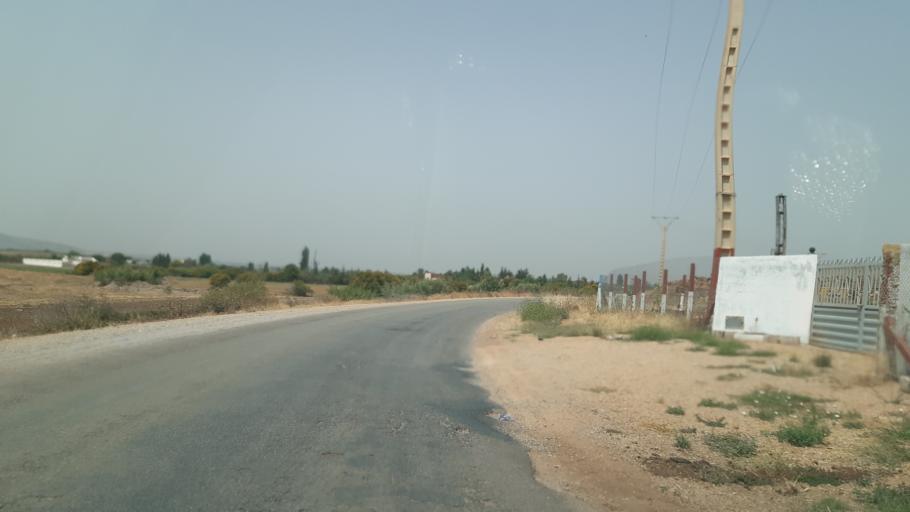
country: MA
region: Fes-Boulemane
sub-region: Fes
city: Oulad Tayeb
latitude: 33.8394
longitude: -5.1200
